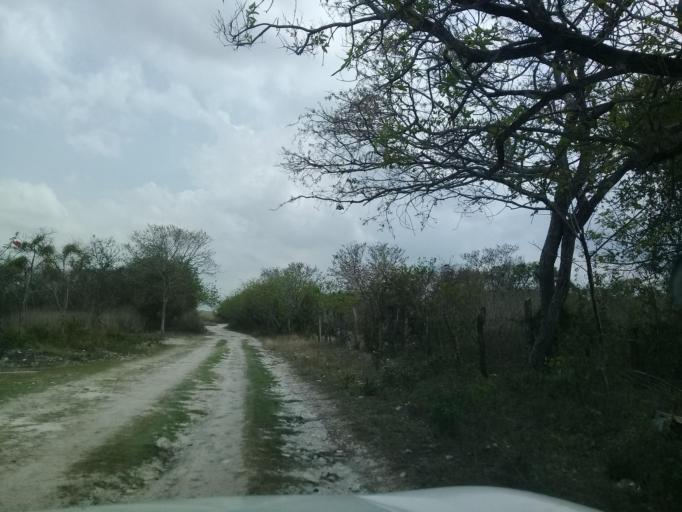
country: MX
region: Veracruz
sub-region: Emiliano Zapata
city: Plan del Rio
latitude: 19.3550
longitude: -96.6611
